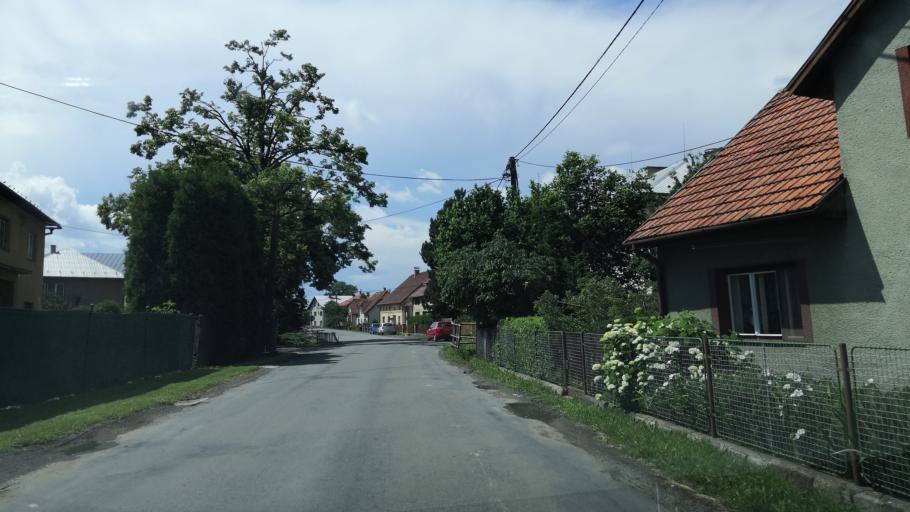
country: CZ
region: Zlin
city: Zasova
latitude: 49.4580
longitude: 18.0605
